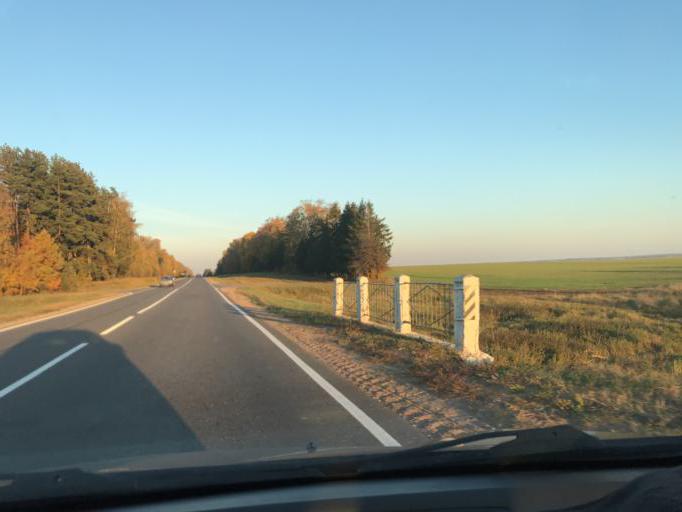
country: BY
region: Minsk
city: Staryya Darohi
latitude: 53.0604
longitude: 28.4842
